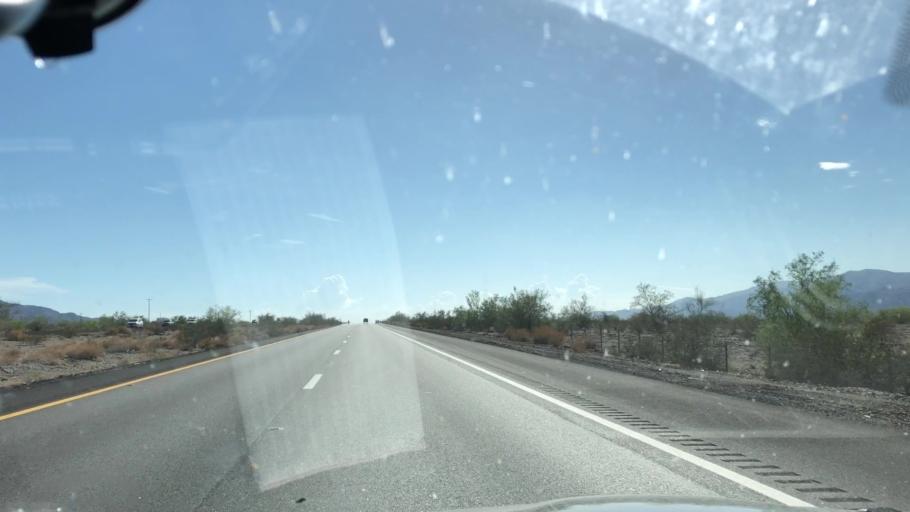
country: US
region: California
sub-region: Imperial County
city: Niland
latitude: 33.6897
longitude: -115.5109
